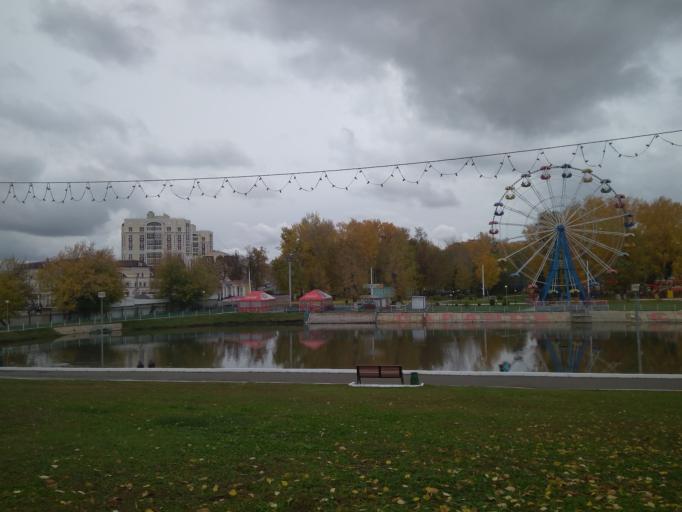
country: RU
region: Mordoviya
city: Saransk
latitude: 54.1791
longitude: 45.1848
